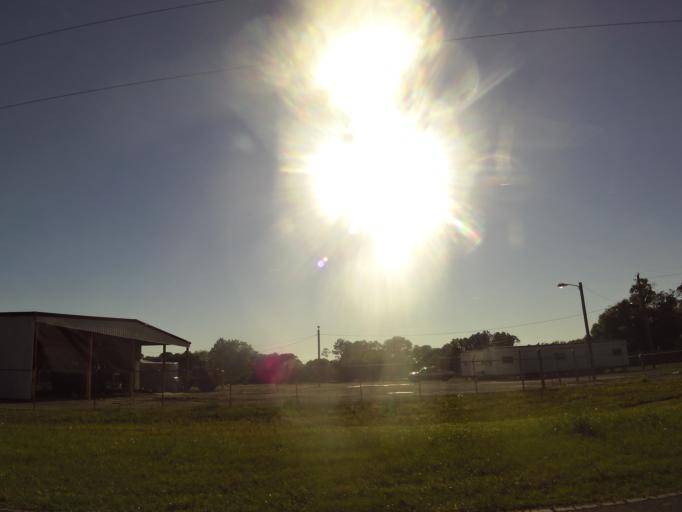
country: US
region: Florida
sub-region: Bradford County
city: Starke
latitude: 29.9296
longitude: -82.1147
